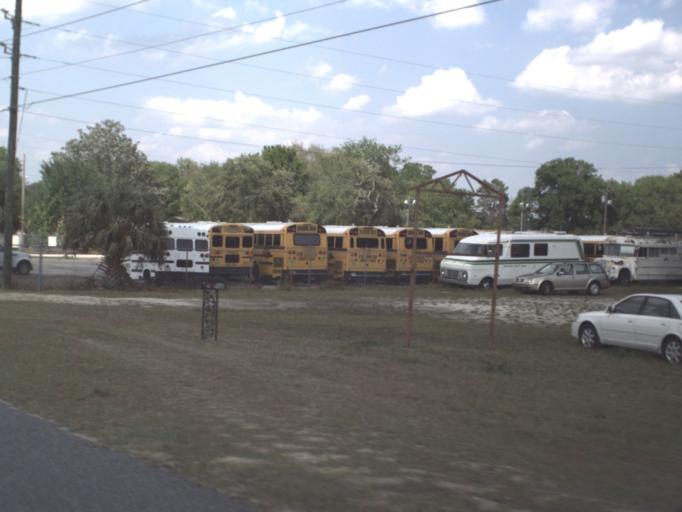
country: US
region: Florida
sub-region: Lake County
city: Tavares
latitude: 28.7758
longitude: -81.7487
